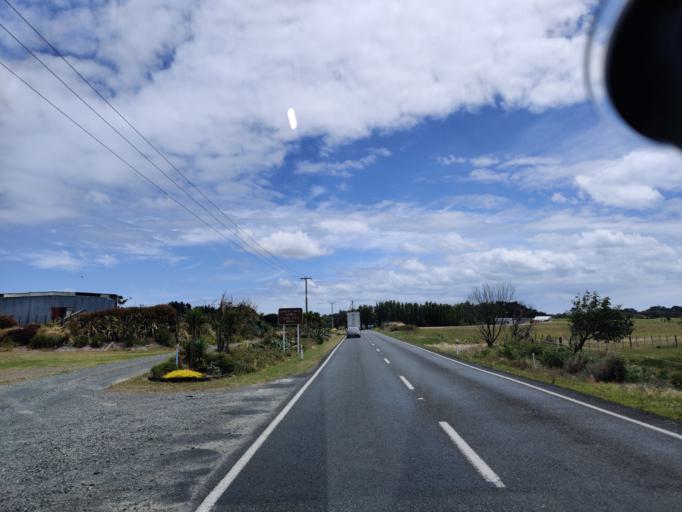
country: NZ
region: Northland
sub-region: Far North District
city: Kaitaia
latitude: -34.8369
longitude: 173.1340
